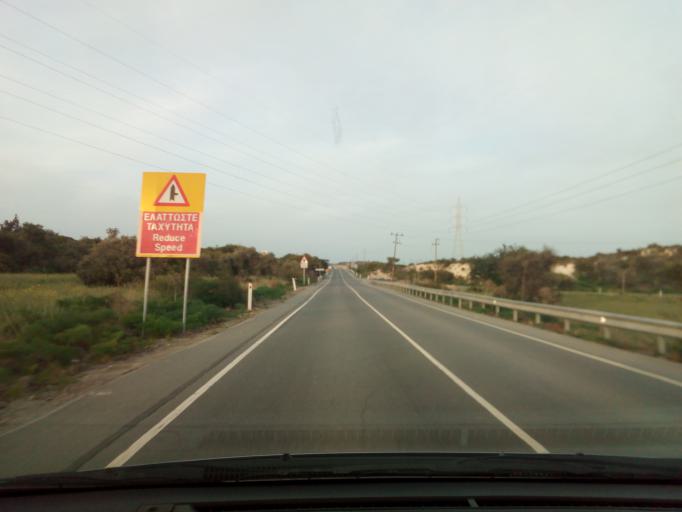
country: CY
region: Limassol
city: Pyrgos
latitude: 34.7293
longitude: 33.2796
